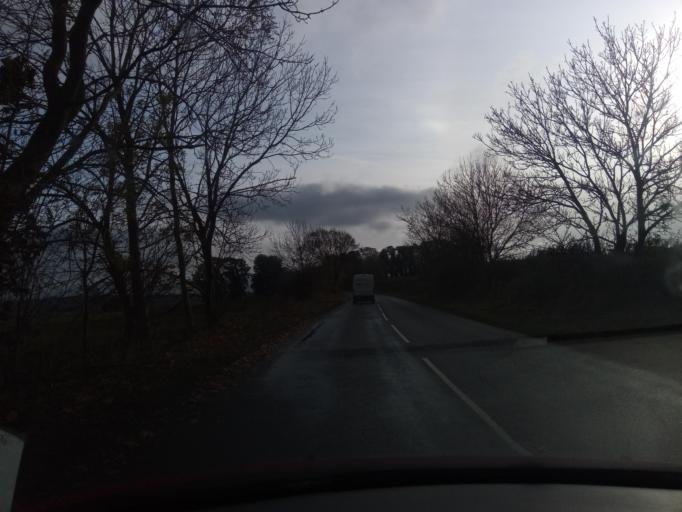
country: GB
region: England
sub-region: Northumberland
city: Birtley
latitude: 55.0472
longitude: -2.1547
